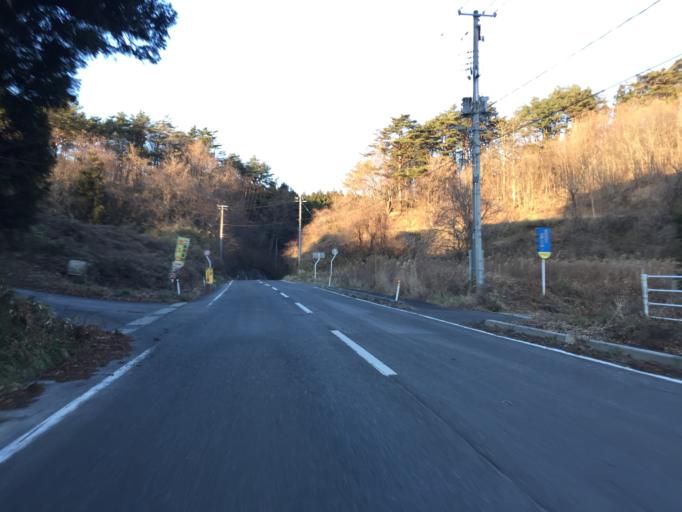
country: JP
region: Fukushima
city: Ishikawa
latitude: 37.2635
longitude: 140.5687
